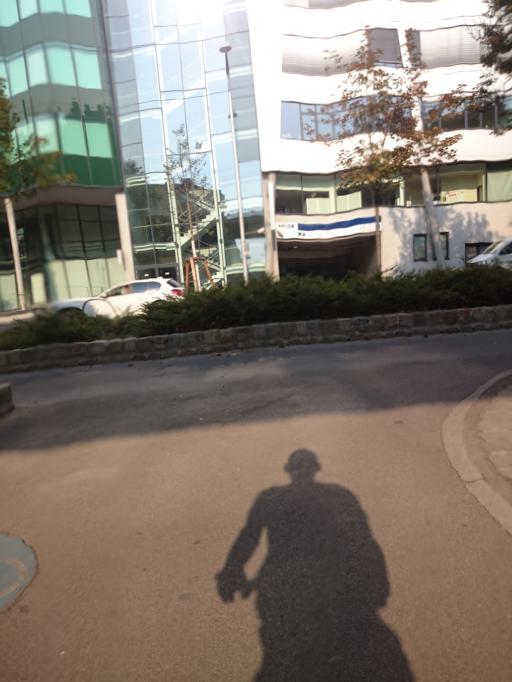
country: AT
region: Vienna
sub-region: Wien Stadt
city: Vienna
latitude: 48.2271
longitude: 16.3500
